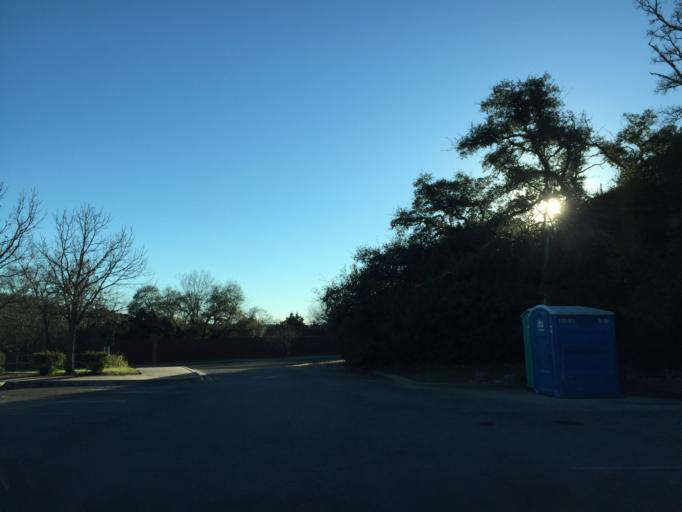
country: US
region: Texas
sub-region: Williamson County
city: Jollyville
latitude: 30.4316
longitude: -97.7818
